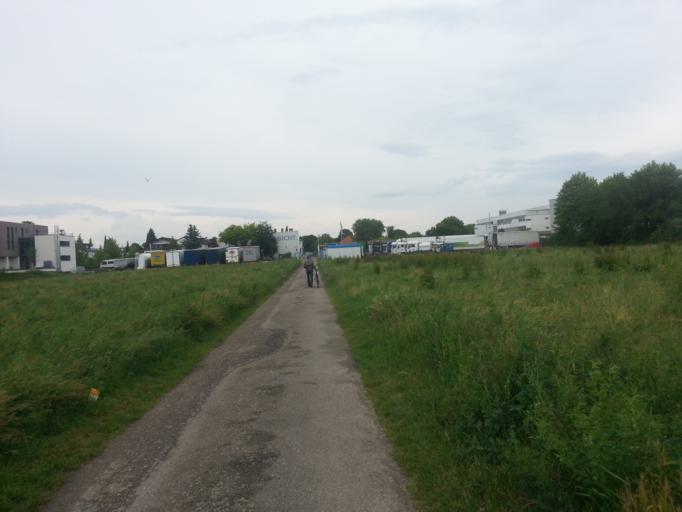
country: DE
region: Baden-Wuerttemberg
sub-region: Karlsruhe Region
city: Ilvesheim
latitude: 49.4725
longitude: 8.5307
